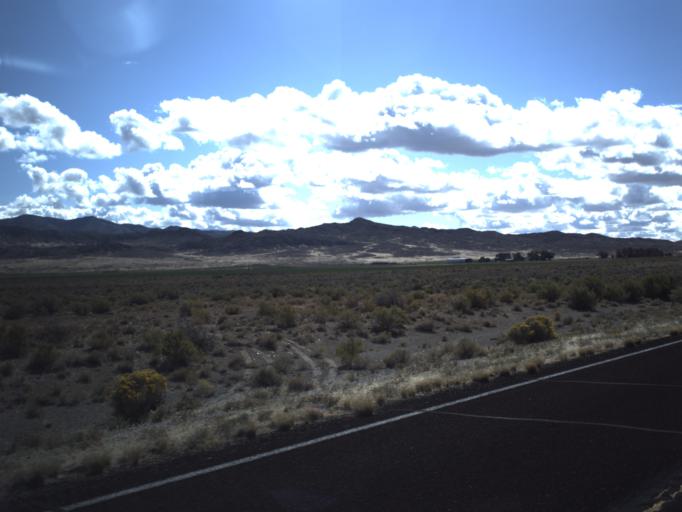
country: US
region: Nevada
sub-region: White Pine County
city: McGill
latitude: 38.9589
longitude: -114.0335
